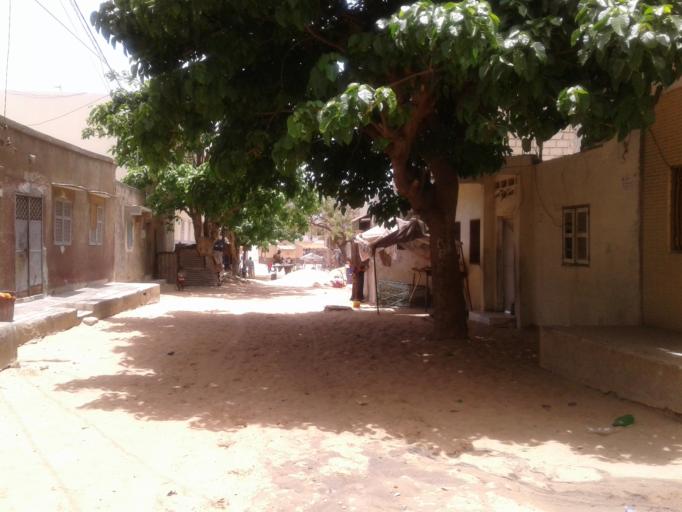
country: SN
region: Dakar
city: Pikine
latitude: 14.7830
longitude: -17.3752
